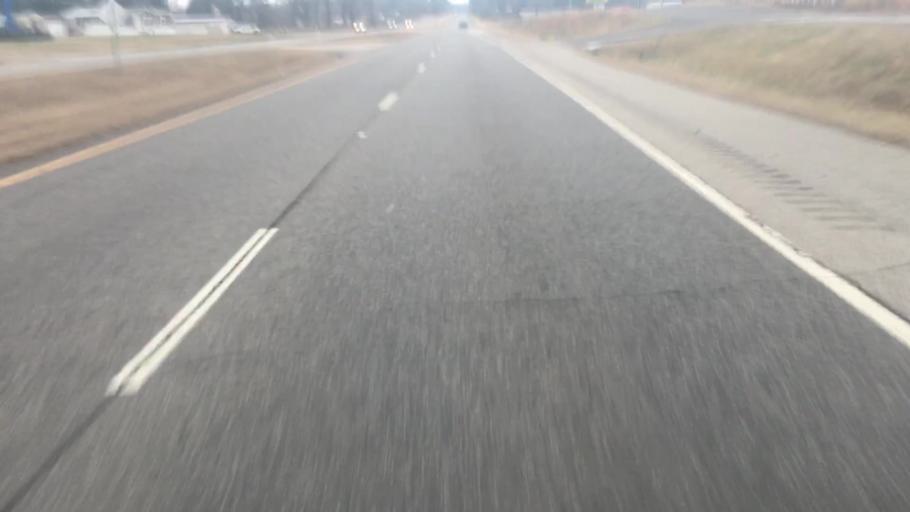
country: US
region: Alabama
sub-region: Walker County
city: Jasper
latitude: 33.8323
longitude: -87.2145
